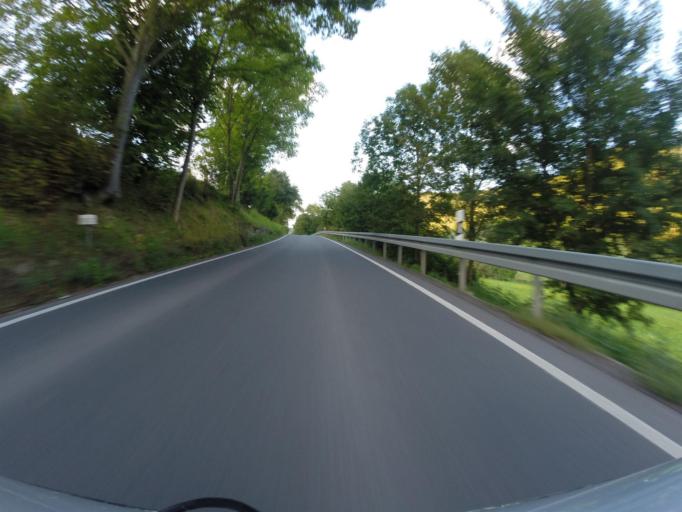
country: DE
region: Thuringia
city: Bucha
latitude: 50.8933
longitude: 11.5464
